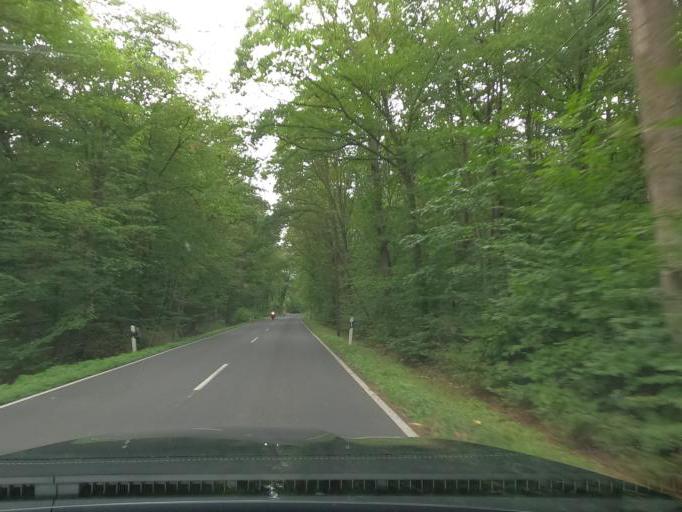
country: DE
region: Lower Saxony
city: Sehnde
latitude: 52.3069
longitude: 9.8966
